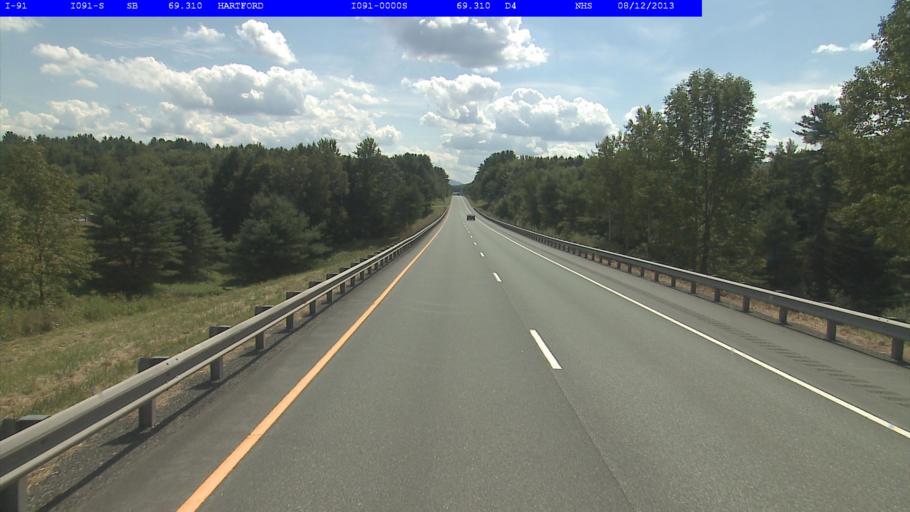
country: US
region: Vermont
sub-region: Windsor County
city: White River Junction
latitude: 43.6329
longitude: -72.3403
